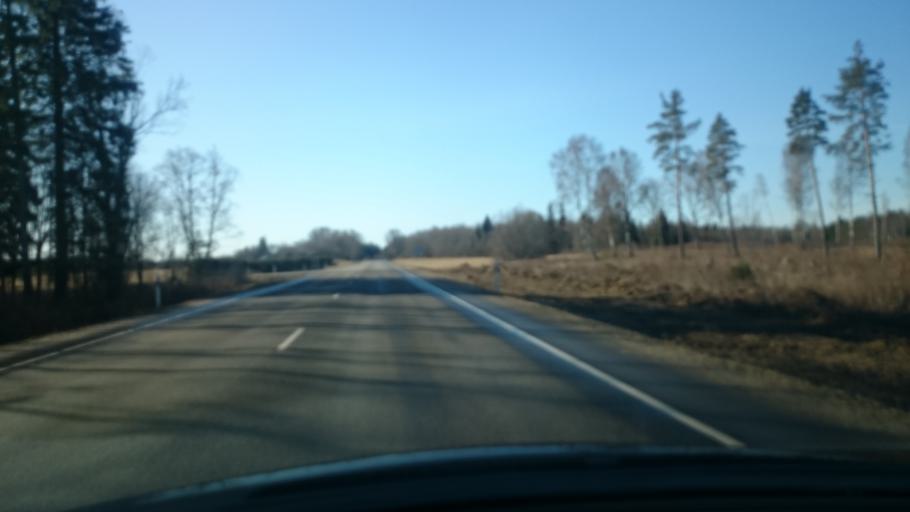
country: EE
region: Harju
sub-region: Saku vald
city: Saku
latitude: 59.2615
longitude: 24.7409
